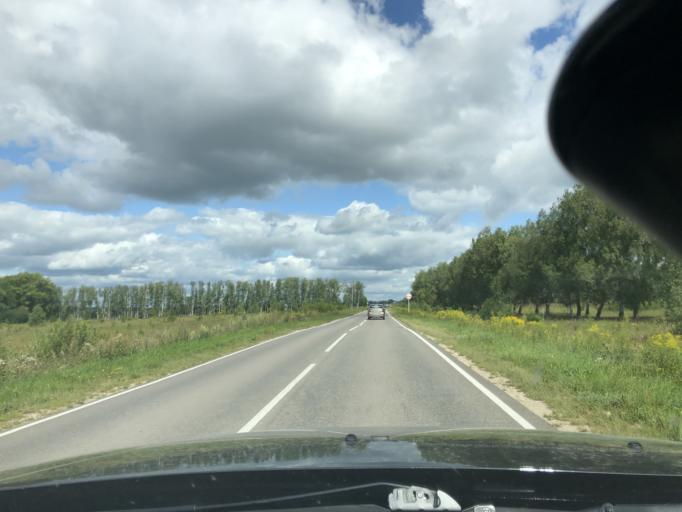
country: RU
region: Tula
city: Yasnogorsk
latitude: 54.4587
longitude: 37.7098
